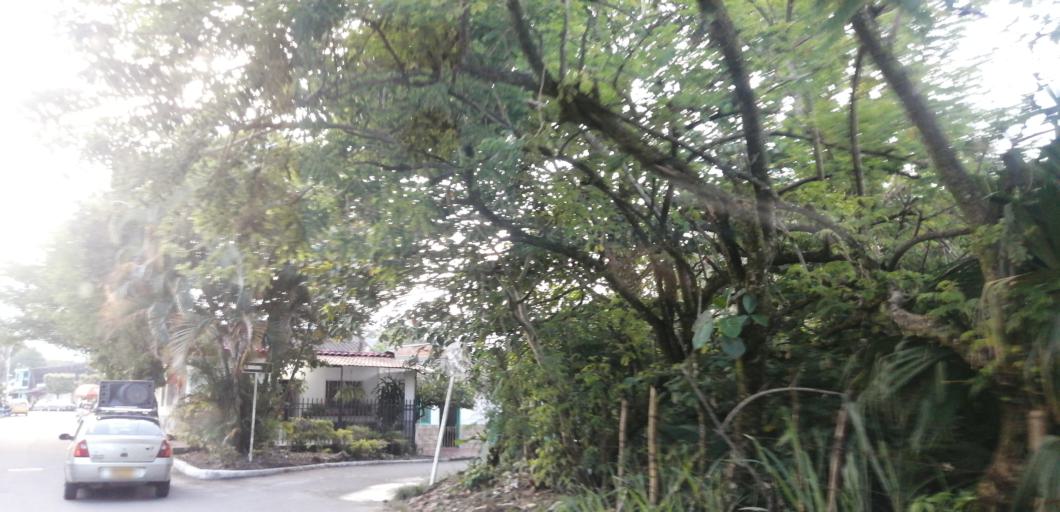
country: CO
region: Meta
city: Acacias
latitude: 3.9880
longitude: -73.7585
